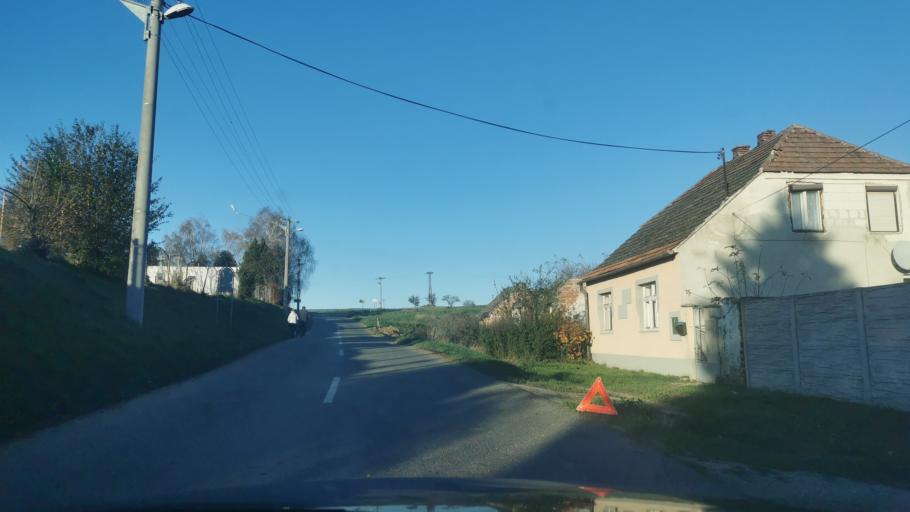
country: SK
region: Trnavsky
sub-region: Okres Skalica
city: Skalica
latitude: 48.7739
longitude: 17.2828
